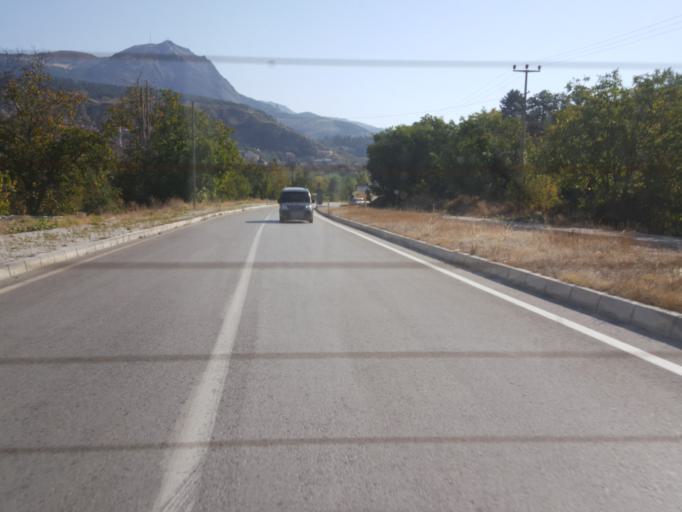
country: TR
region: Corum
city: Iskilip
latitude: 40.7377
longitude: 34.4555
